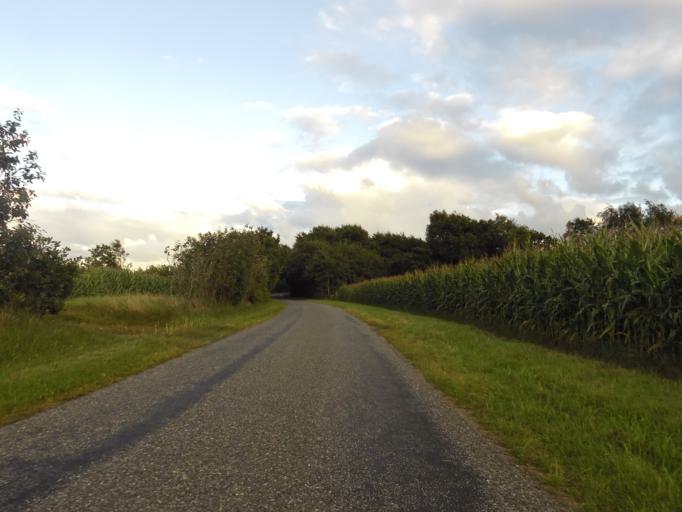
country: DK
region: South Denmark
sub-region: Esbjerg Kommune
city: Ribe
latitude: 55.3039
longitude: 8.7772
